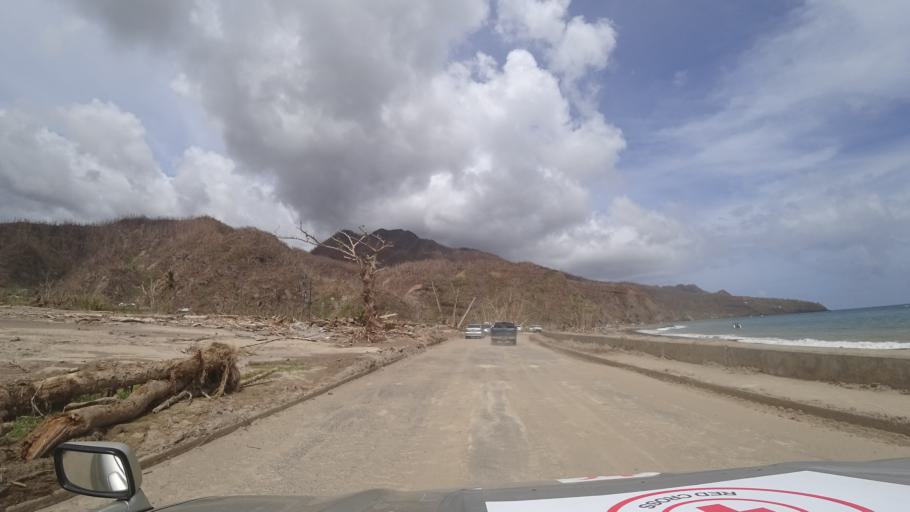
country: DM
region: Saint Patrick
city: Berekua
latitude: 15.2428
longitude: -61.3109
